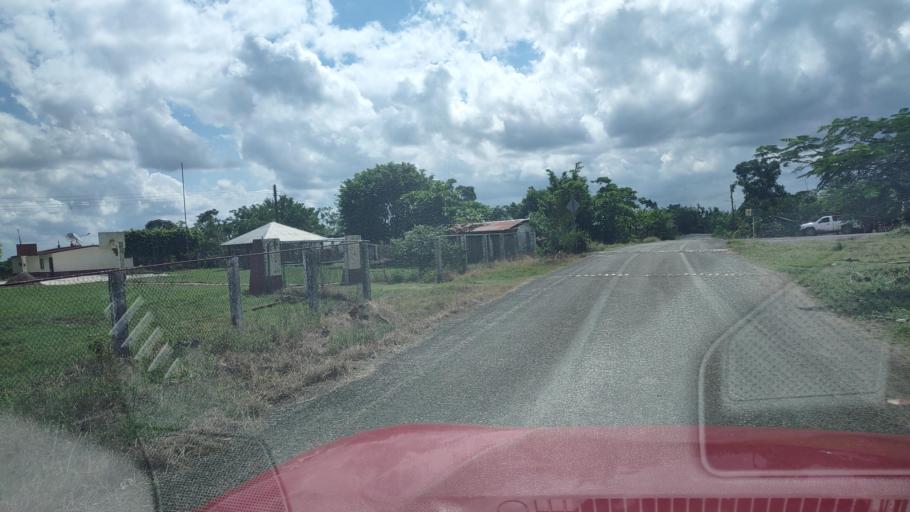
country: MX
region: Puebla
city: San Jose Acateno
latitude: 20.2728
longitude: -97.1298
